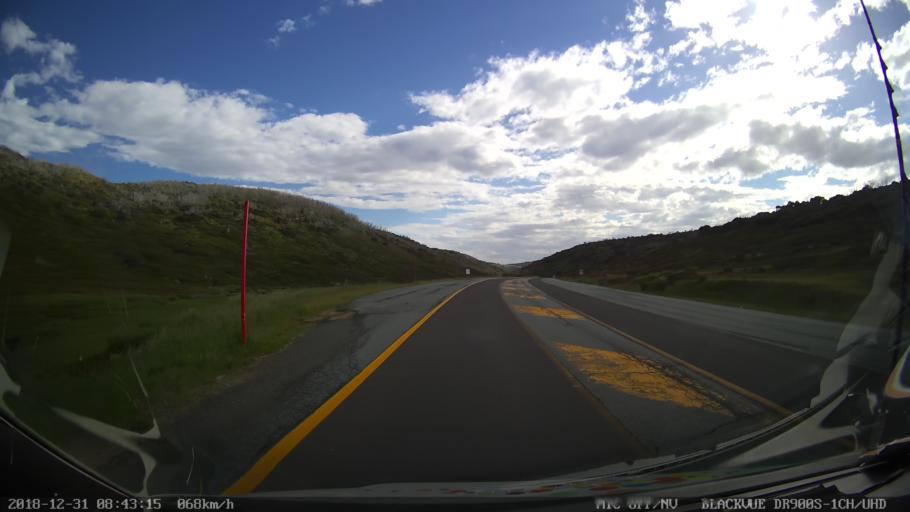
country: AU
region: New South Wales
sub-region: Snowy River
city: Jindabyne
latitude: -36.3903
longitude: 148.4424
